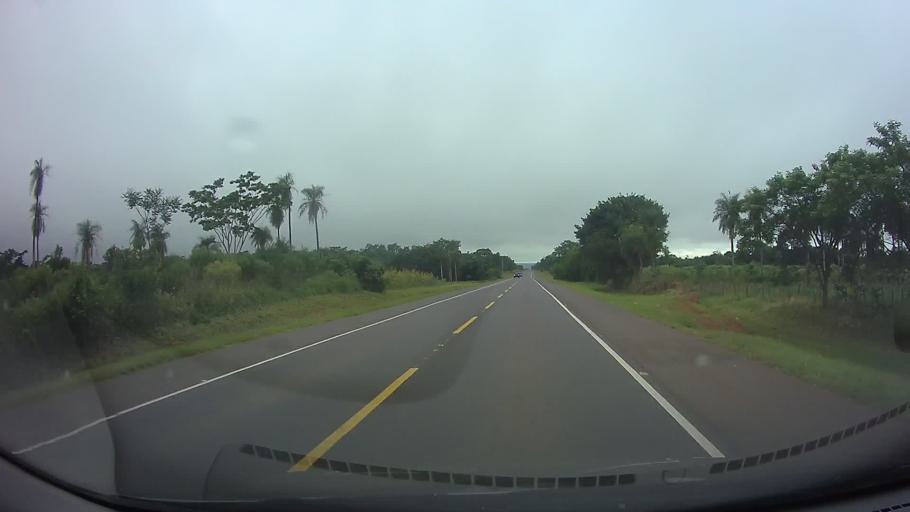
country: PY
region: Paraguari
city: Paraguari
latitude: -25.6151
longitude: -57.1793
